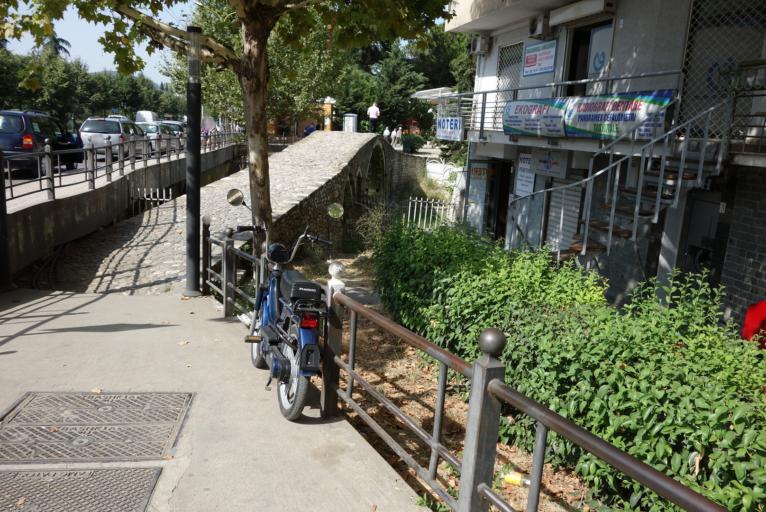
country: AL
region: Tirane
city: Tirana
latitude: 41.3266
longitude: 19.8263
